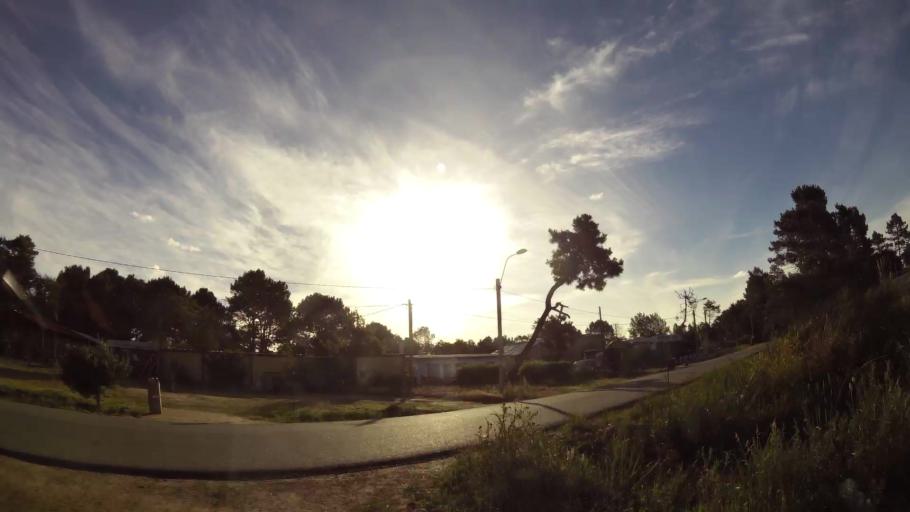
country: UY
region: Canelones
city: Empalme Olmos
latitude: -34.7699
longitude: -55.8602
